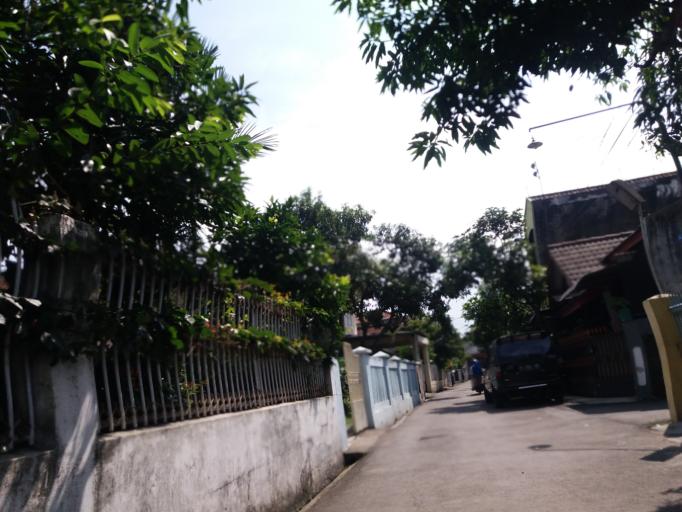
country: ID
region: West Java
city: Bandung
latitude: -6.9215
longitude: 107.6496
